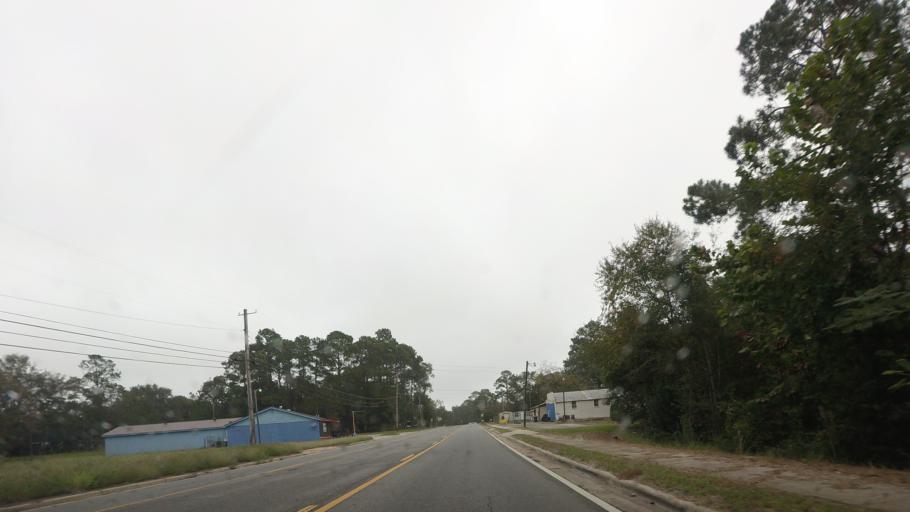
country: US
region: Georgia
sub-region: Ben Hill County
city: Fitzgerald
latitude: 31.7274
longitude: -83.2495
